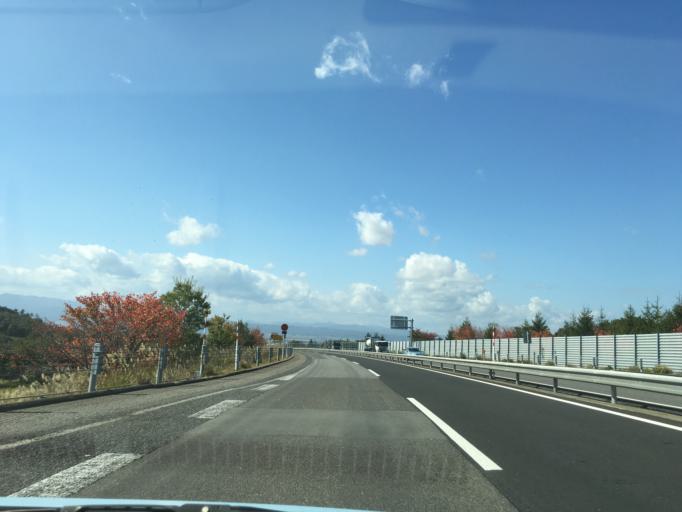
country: JP
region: Fukushima
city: Kitakata
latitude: 37.5509
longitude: 139.9689
